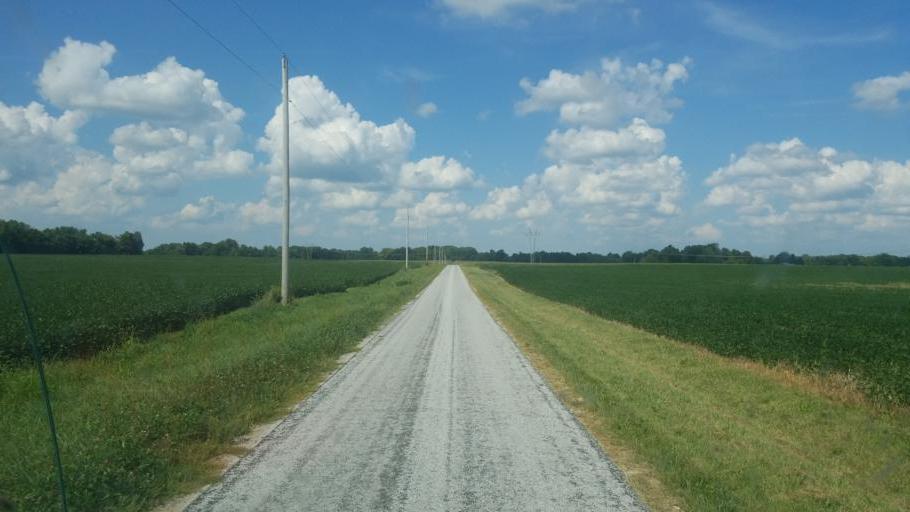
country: US
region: Ohio
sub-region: Wyandot County
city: Carey
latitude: 40.9657
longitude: -83.2470
